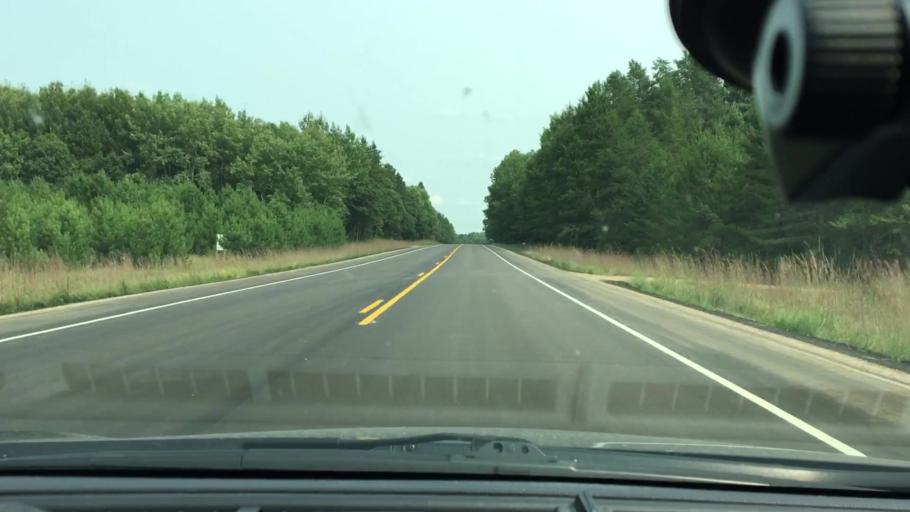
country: US
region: Minnesota
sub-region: Crow Wing County
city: Nisswa
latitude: 46.5297
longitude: -94.2409
